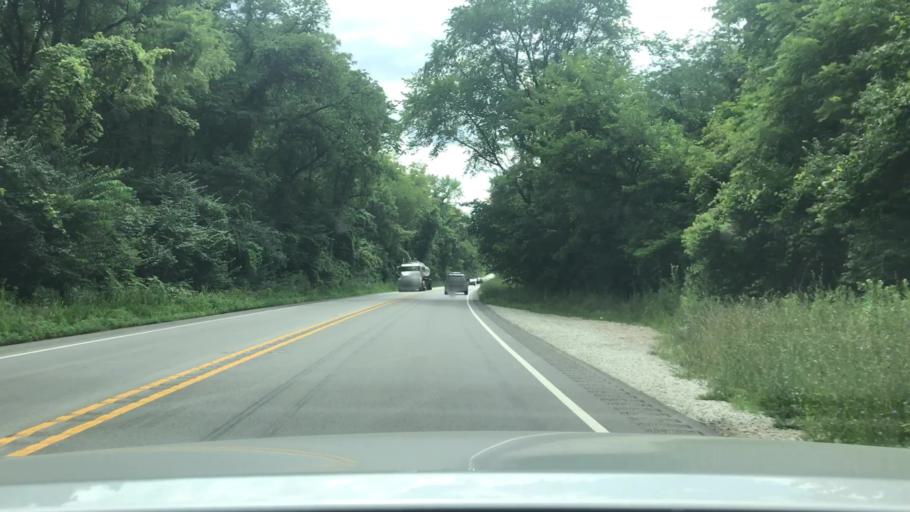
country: US
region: Illinois
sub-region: DuPage County
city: Burr Ridge
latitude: 41.7036
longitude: -87.9258
